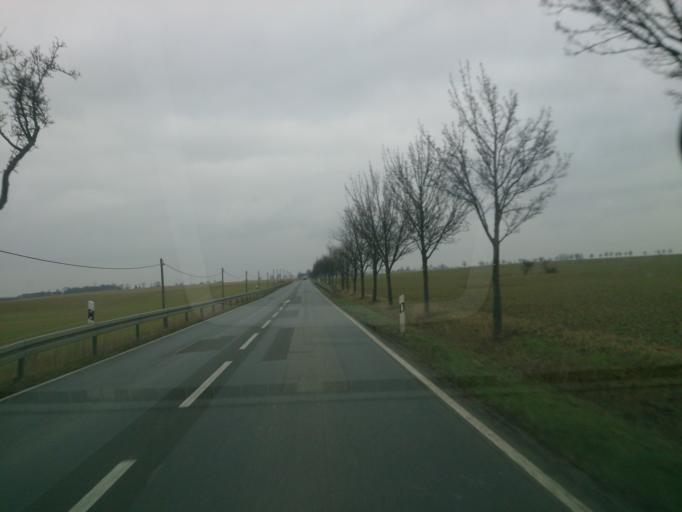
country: DE
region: Mecklenburg-Vorpommern
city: Borrentin
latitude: 53.7662
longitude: 12.9374
